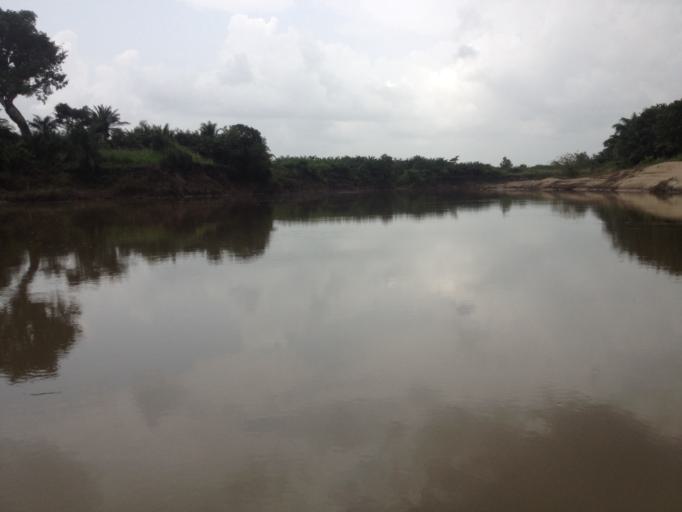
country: BJ
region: Mono
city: Lokossa
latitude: 6.5022
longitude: 1.6960
